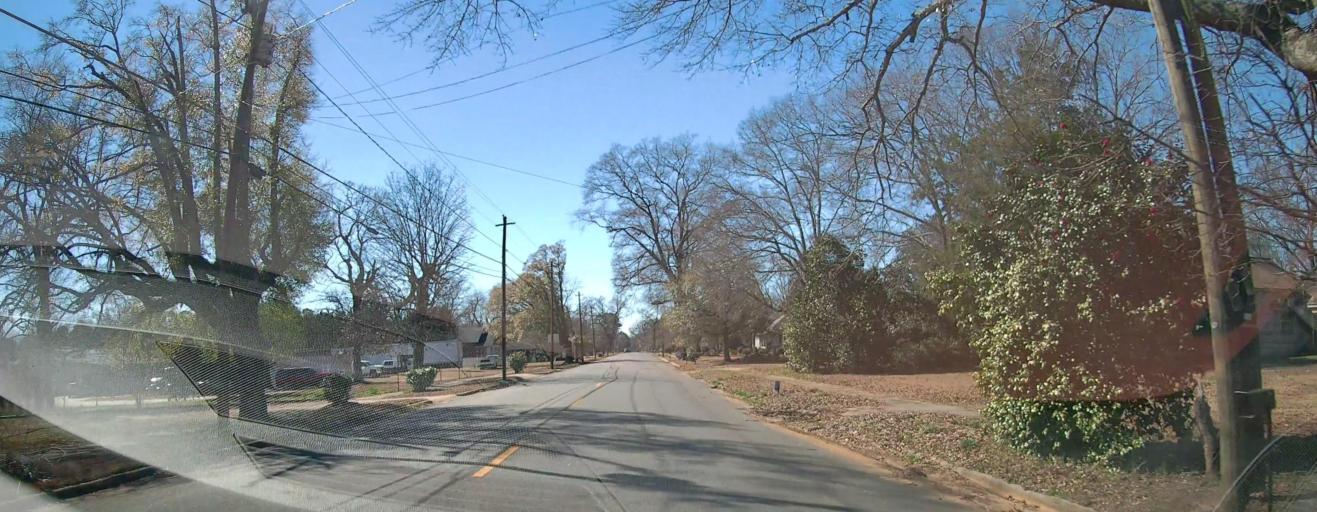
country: US
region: Georgia
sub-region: Macon County
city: Marshallville
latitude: 32.4564
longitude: -83.9459
